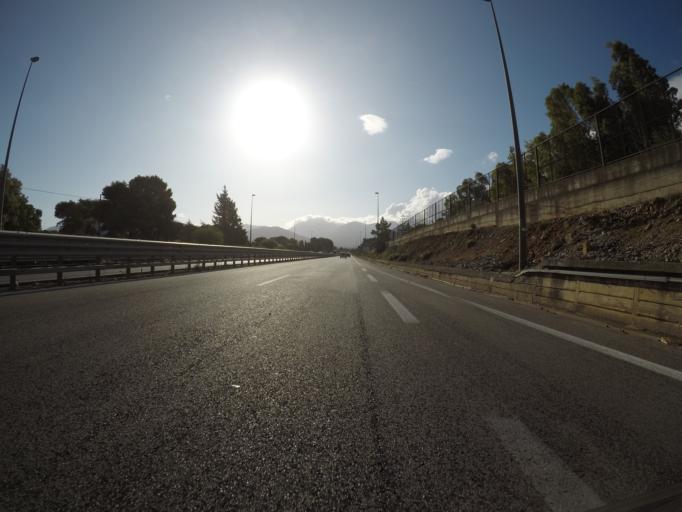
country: IT
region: Sicily
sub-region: Palermo
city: Carini
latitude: 38.1735
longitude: 13.1586
